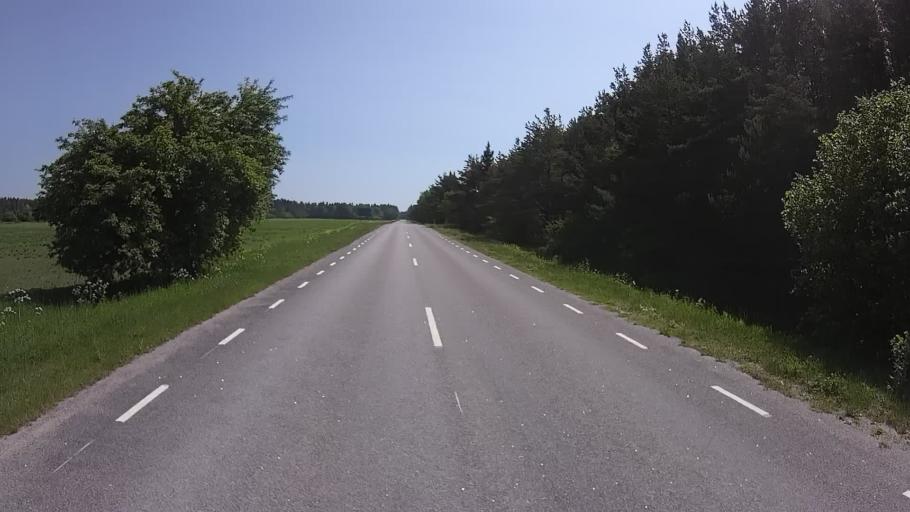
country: EE
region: Saare
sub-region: Kuressaare linn
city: Kuressaare
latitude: 58.3624
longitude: 22.0587
